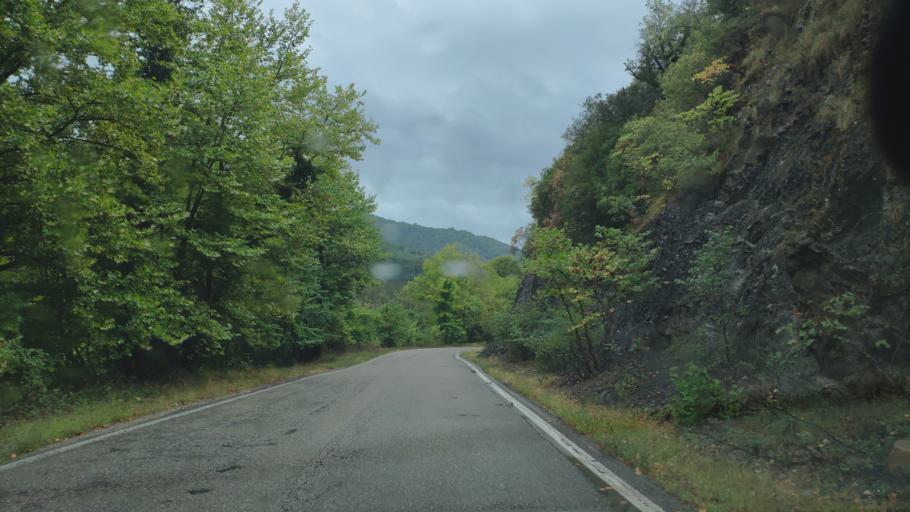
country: GR
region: West Greece
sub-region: Nomos Aitolias kai Akarnanias
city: Krikellos
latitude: 38.9588
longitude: 21.3365
